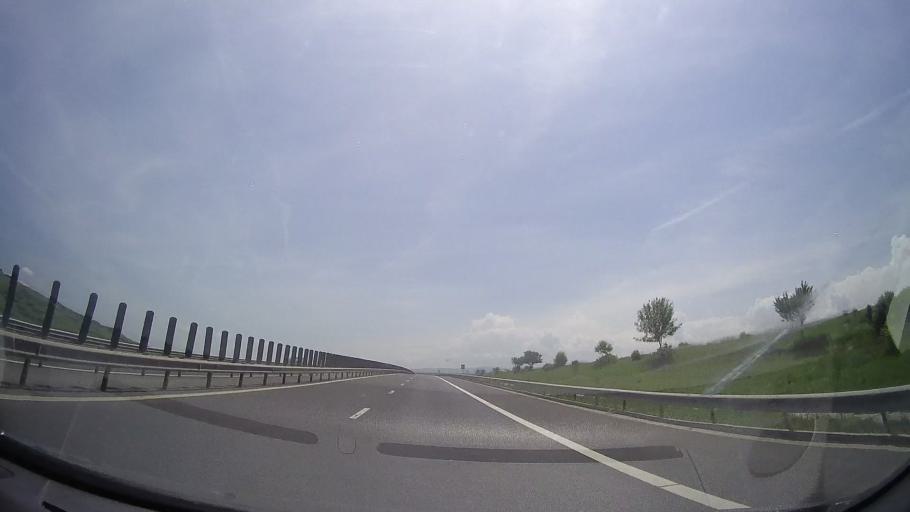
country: RO
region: Alba
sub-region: Municipiul Sebes
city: Sebes
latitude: 45.9387
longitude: 23.5980
